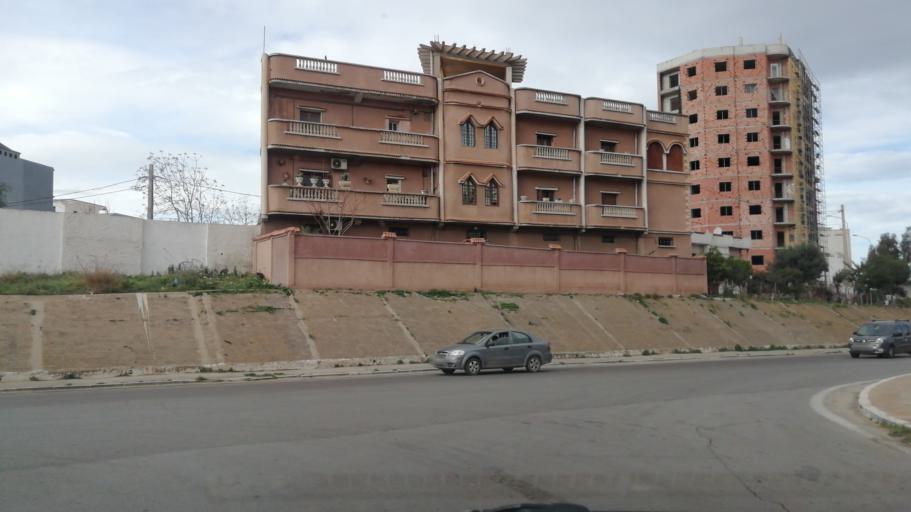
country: DZ
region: Oran
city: Oran
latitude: 35.7012
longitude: -0.6136
